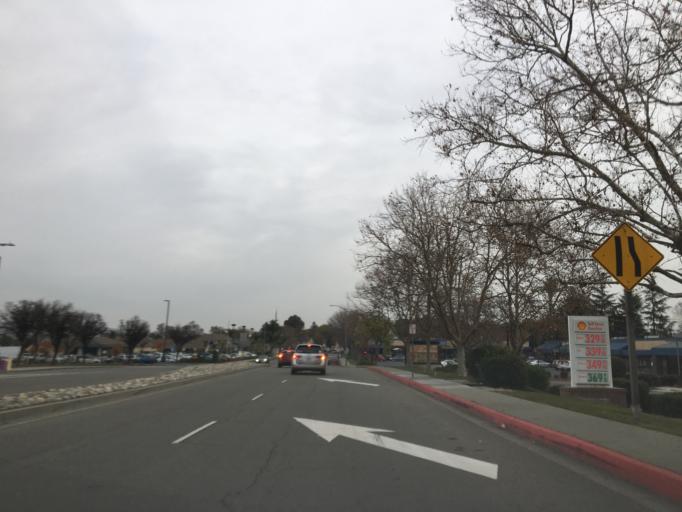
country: US
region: California
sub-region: Alameda County
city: Pleasanton
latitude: 37.7002
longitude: -121.8716
